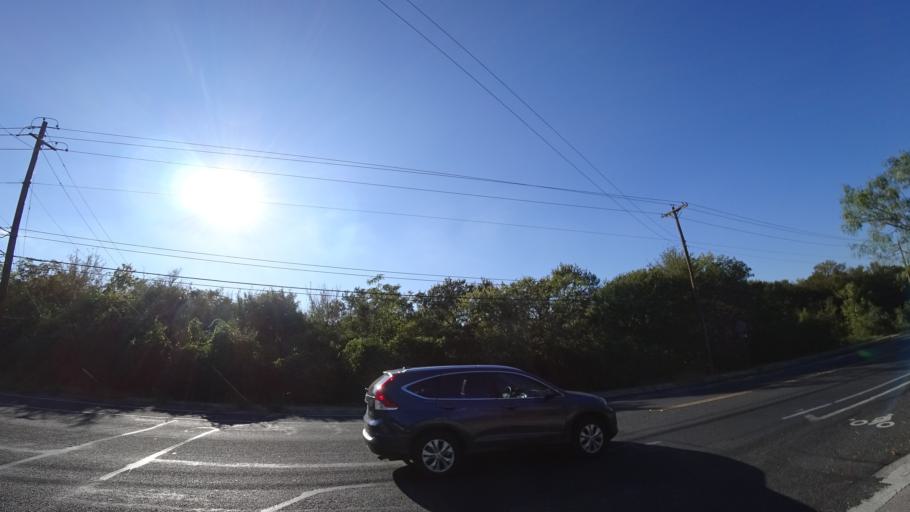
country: US
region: Texas
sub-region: Travis County
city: Austin
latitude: 30.2251
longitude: -97.7349
